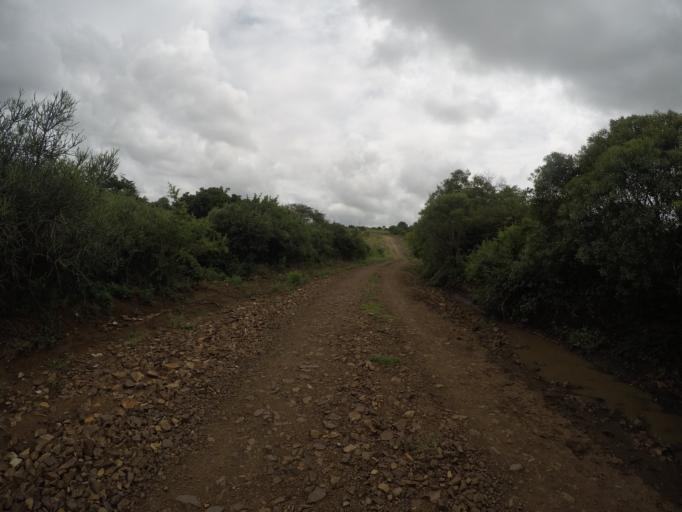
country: ZA
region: KwaZulu-Natal
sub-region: uThungulu District Municipality
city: Empangeni
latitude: -28.5842
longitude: 31.8680
